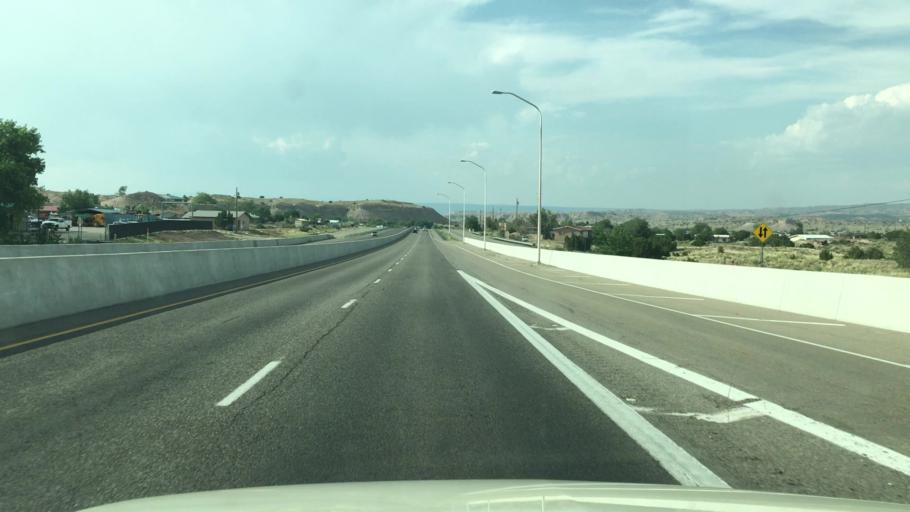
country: US
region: New Mexico
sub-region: Santa Fe County
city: El Valle de Arroyo Seco
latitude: 35.9319
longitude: -106.0184
